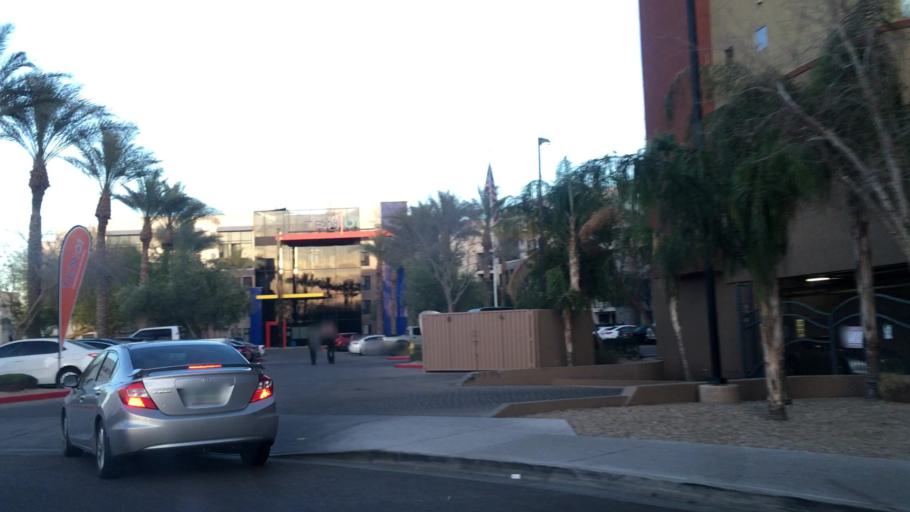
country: US
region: Arizona
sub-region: Maricopa County
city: Tempe
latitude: 33.4340
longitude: -111.9249
